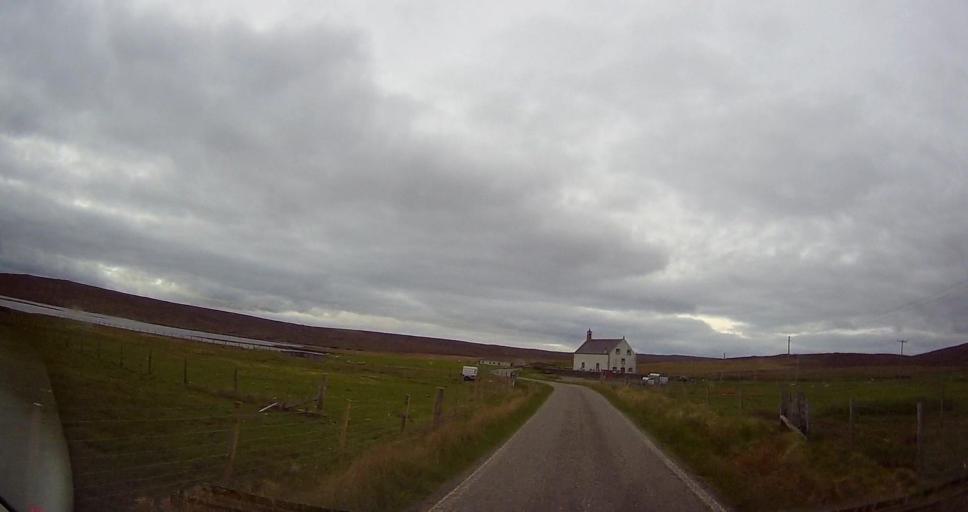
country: GB
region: Scotland
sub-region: Shetland Islands
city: Shetland
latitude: 60.5033
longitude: -1.0987
